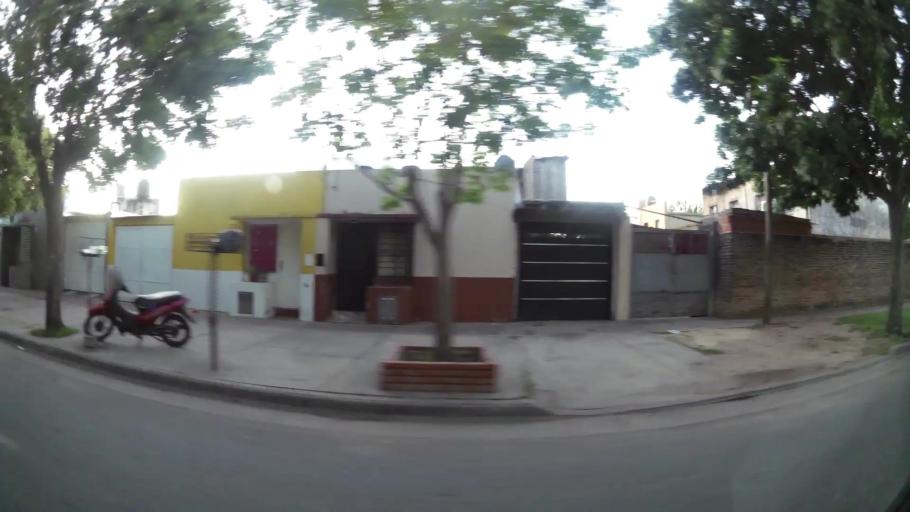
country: AR
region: Santa Fe
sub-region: Departamento de Rosario
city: Rosario
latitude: -32.9695
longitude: -60.6882
